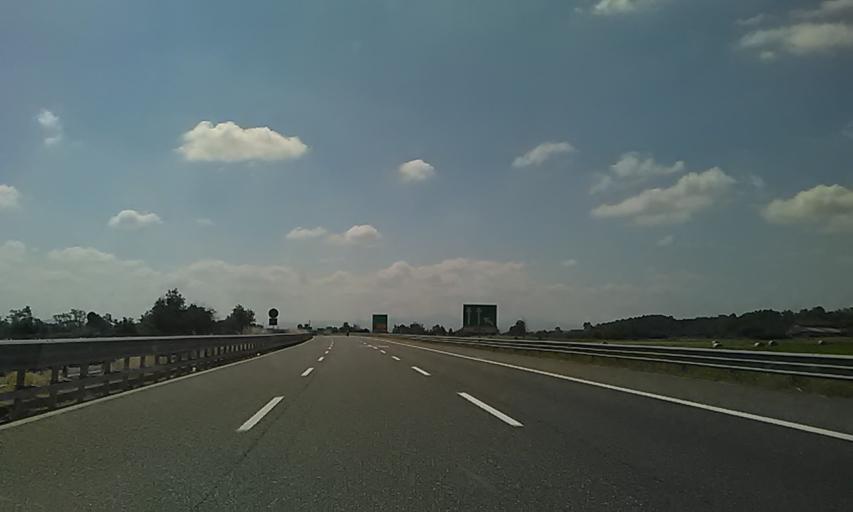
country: IT
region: Piedmont
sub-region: Provincia di Alessandria
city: Predosa
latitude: 44.7658
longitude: 8.6351
